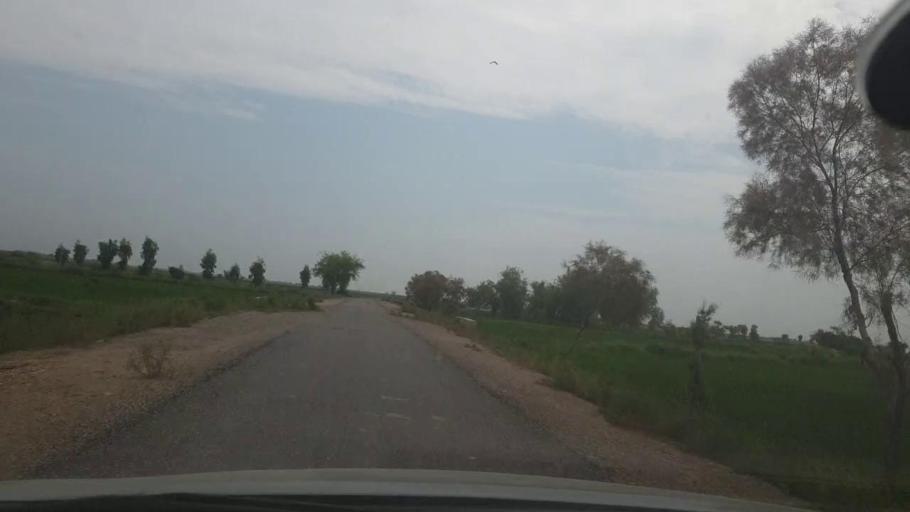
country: PK
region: Balochistan
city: Garhi Khairo
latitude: 28.0232
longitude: 68.0436
